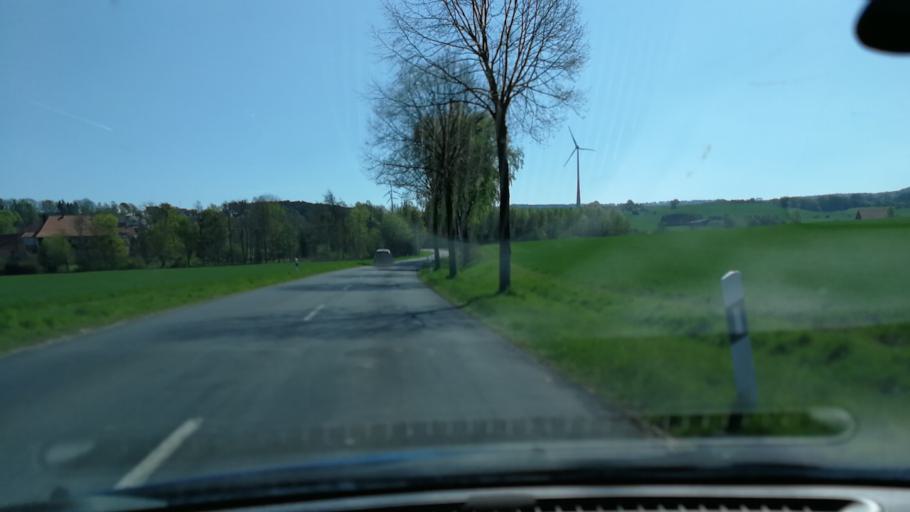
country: DE
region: Lower Saxony
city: Dransfeld
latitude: 51.5203
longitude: 9.7213
